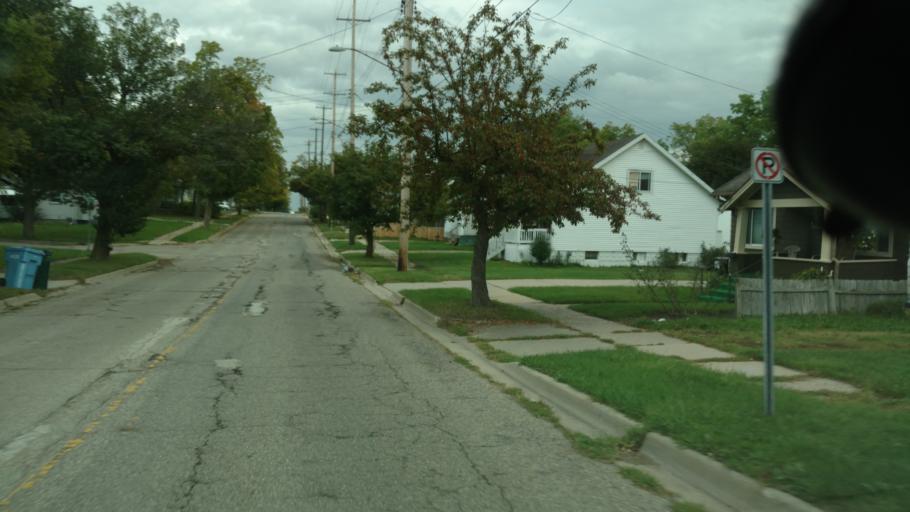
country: US
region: Michigan
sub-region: Ingham County
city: Lansing
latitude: 42.7233
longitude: -84.5769
